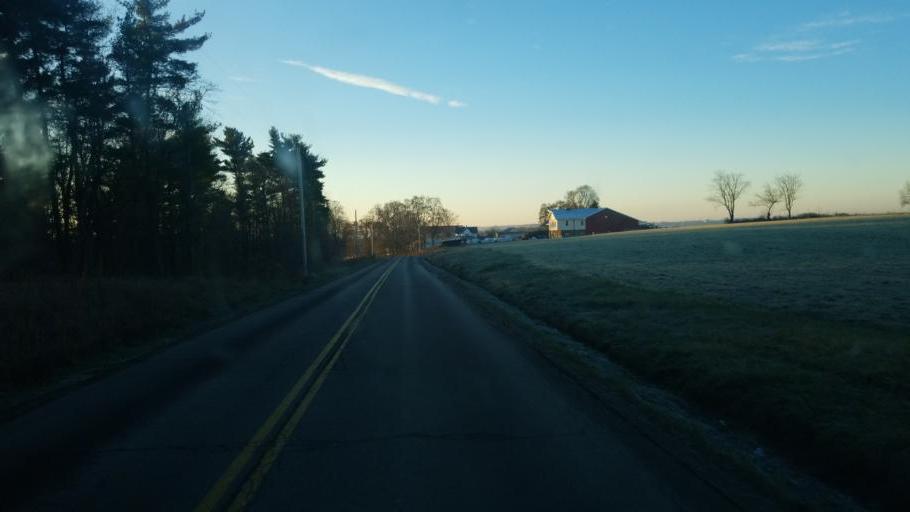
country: US
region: Ohio
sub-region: Holmes County
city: Millersburg
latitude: 40.6399
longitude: -81.8467
